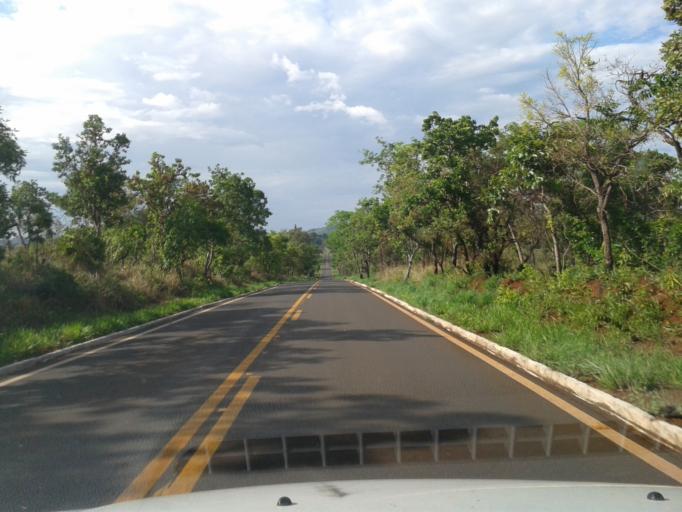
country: BR
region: Minas Gerais
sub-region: Ituiutaba
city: Ituiutaba
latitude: -19.1283
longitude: -49.7733
